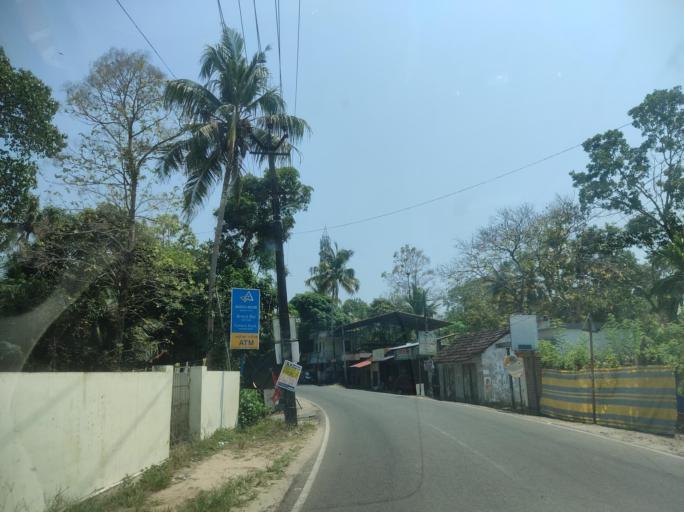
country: IN
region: Kerala
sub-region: Alappuzha
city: Kutiatodu
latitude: 9.7977
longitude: 76.3019
